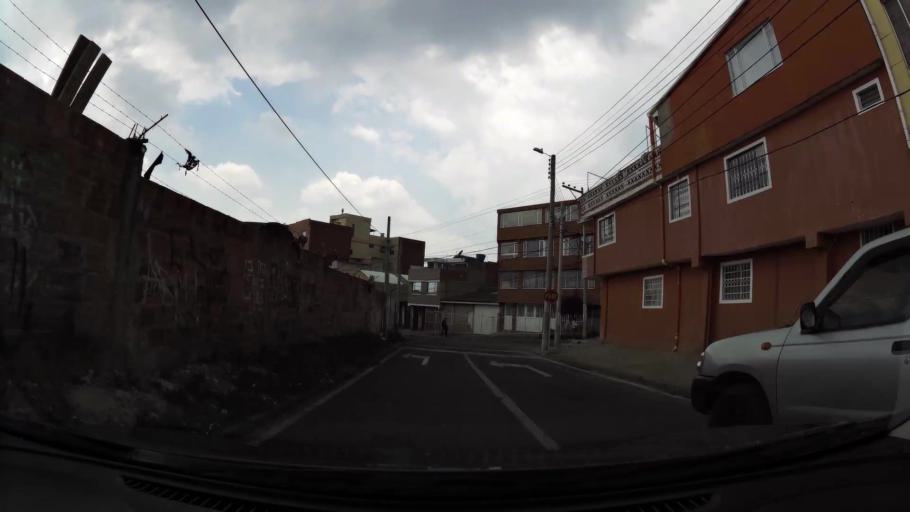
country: CO
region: Cundinamarca
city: La Calera
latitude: 4.7377
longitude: -74.0239
